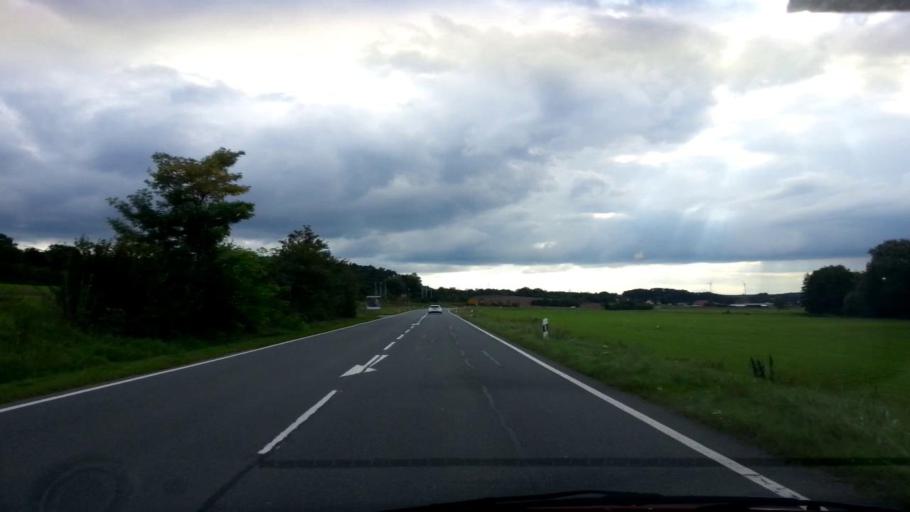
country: DE
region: Bavaria
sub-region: Upper Franconia
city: Schlusselfeld
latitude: 49.7373
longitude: 10.6321
